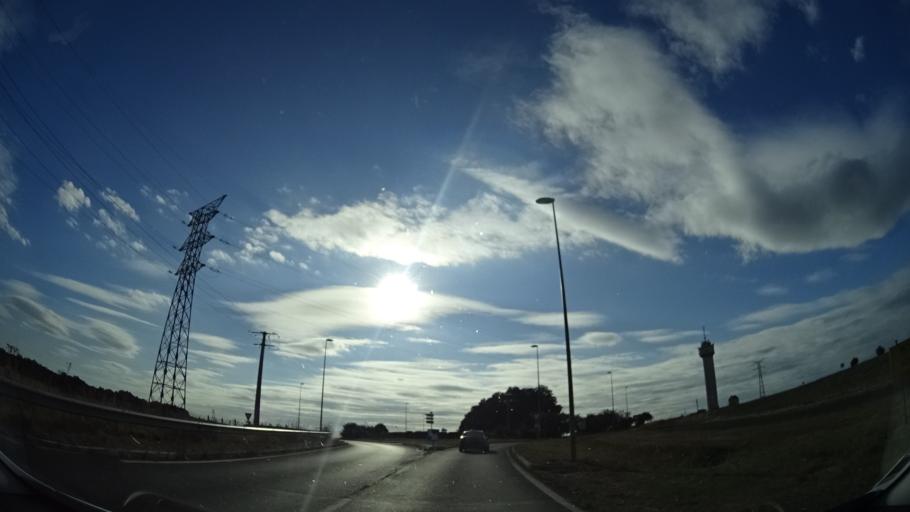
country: FR
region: Centre
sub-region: Departement du Loir-et-Cher
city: Moree
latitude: 47.9042
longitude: 1.2492
